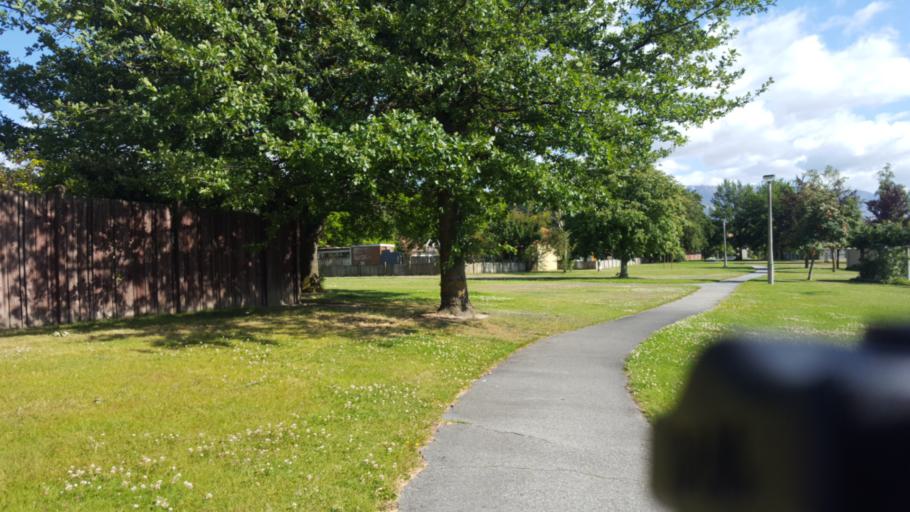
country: NZ
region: Otago
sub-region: Queenstown-Lakes District
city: Wanaka
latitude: -45.0407
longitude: 169.1907
